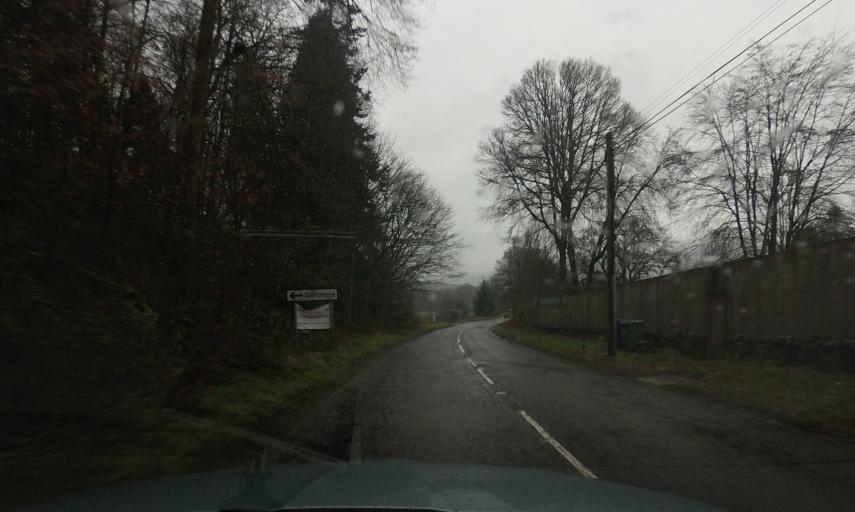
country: GB
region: Scotland
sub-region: Stirling
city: Balfron
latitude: 56.1557
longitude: -4.3640
